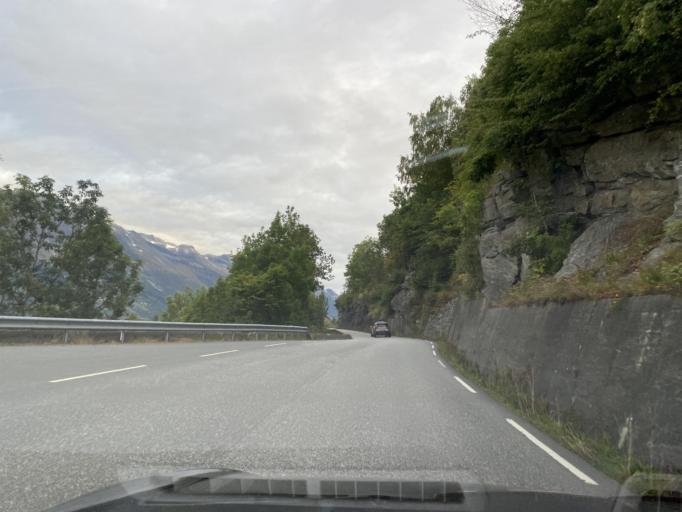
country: NO
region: Hordaland
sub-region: Odda
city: Odda
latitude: 60.2145
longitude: 6.6028
